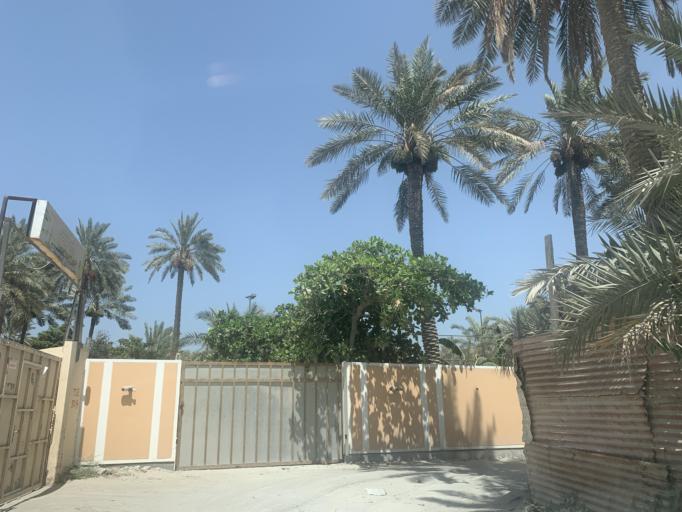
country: BH
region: Manama
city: Jidd Hafs
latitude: 26.2323
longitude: 50.5128
